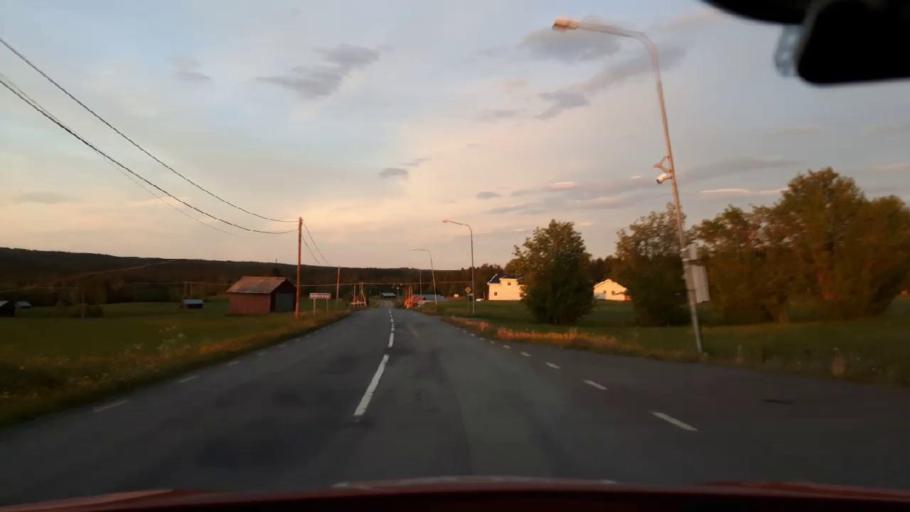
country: SE
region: Jaemtland
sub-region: OEstersunds Kommun
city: Brunflo
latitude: 63.0667
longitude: 14.7930
